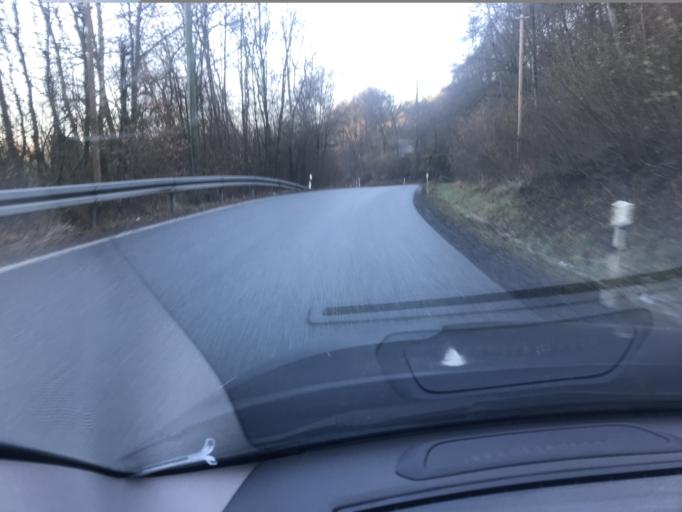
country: DE
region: Rheinland-Pfalz
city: Niedererbach
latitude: 50.4217
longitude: 7.9858
